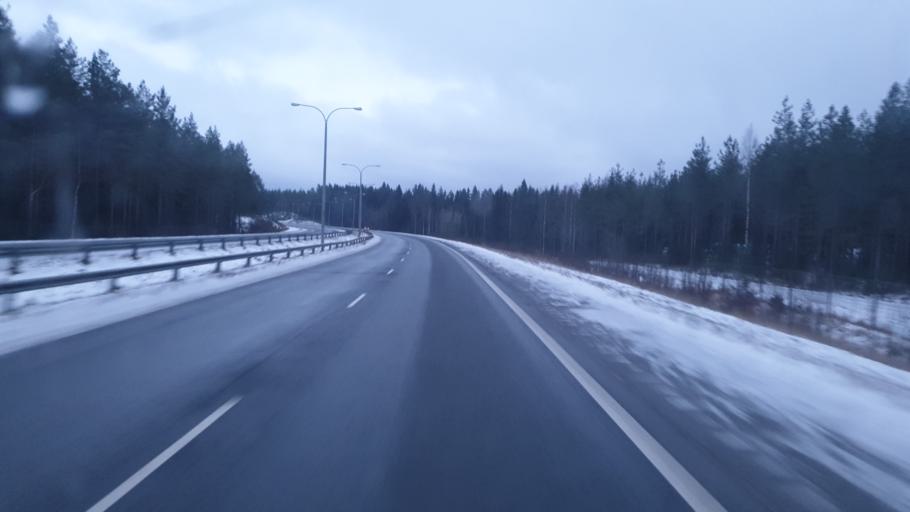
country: FI
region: Northern Savo
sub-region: Kuopio
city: Siilinjaervi
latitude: 63.0064
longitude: 27.6803
